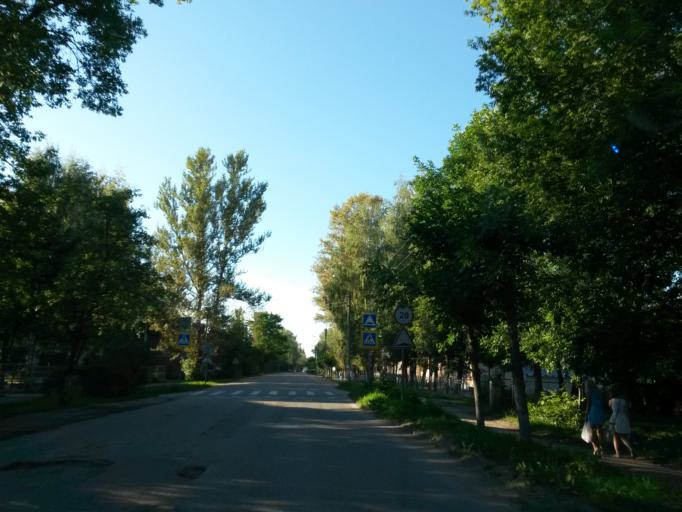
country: RU
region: Jaroslavl
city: Gavrilov-Yam
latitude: 57.3019
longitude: 39.8632
